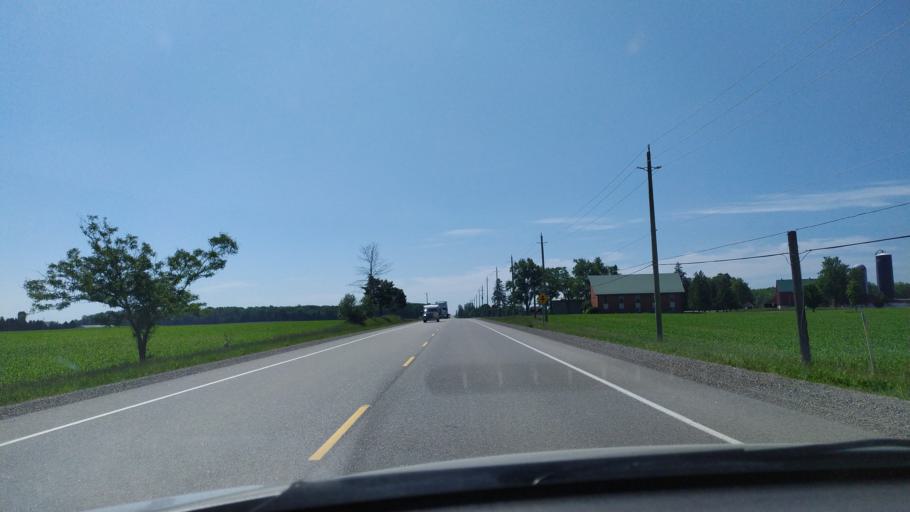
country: CA
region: Ontario
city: Stratford
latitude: 43.4559
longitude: -80.7579
